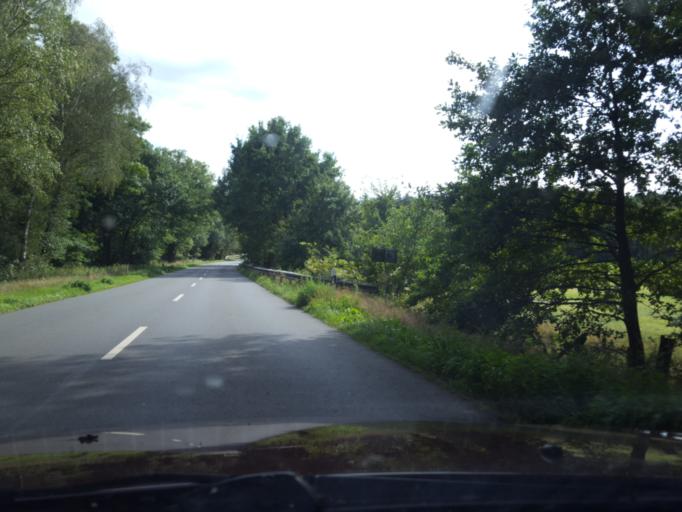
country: DE
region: Lower Saxony
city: Hemsbunde
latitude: 53.0768
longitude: 9.4533
